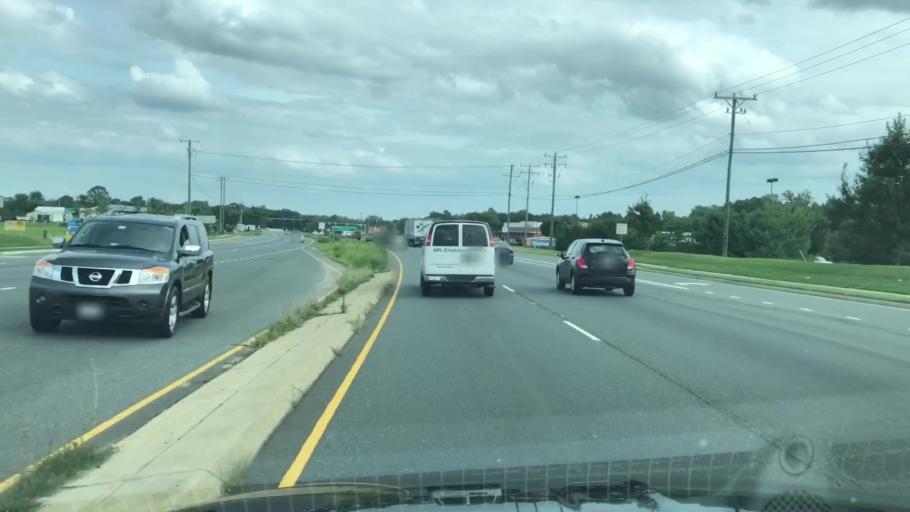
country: US
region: Virginia
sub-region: Stafford County
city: Falmouth
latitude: 38.3727
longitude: -77.5272
